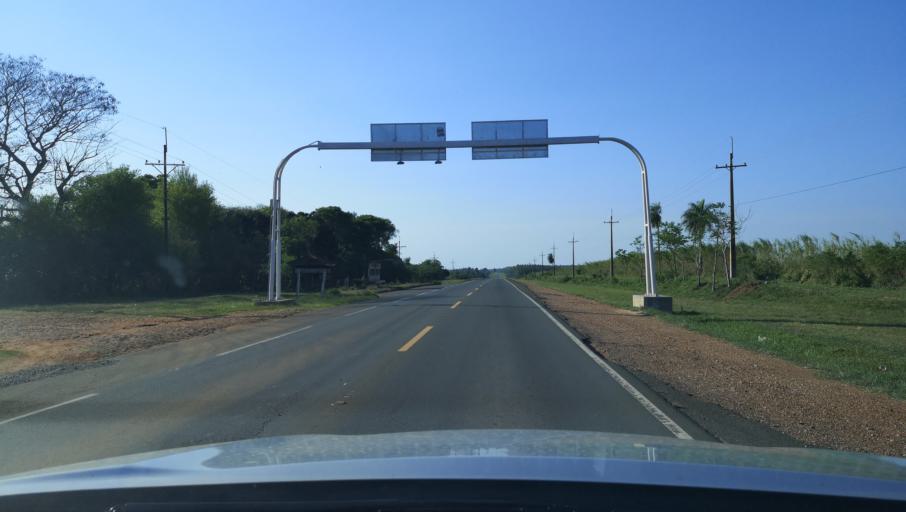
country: PY
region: Misiones
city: Santa Maria
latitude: -26.7823
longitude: -57.0272
